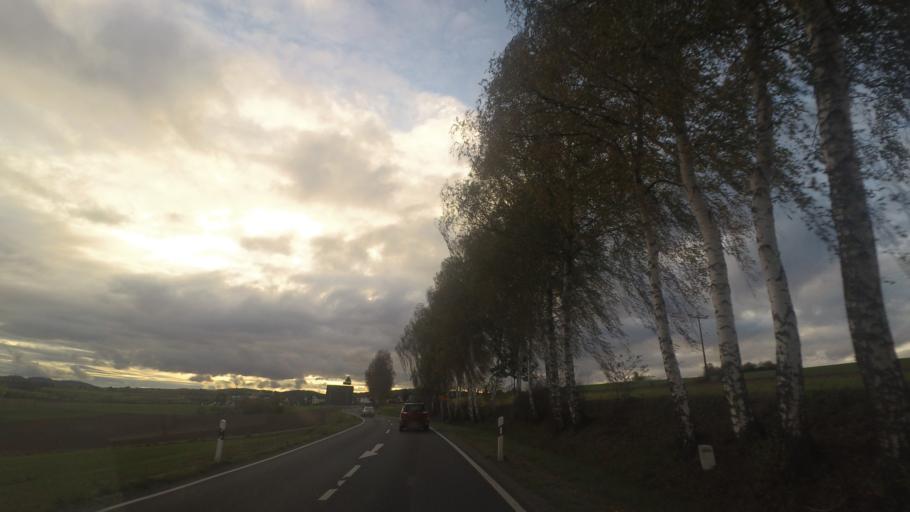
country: DE
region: Hesse
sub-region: Regierungsbezirk Kassel
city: Neuhof
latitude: 50.4546
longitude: 9.5909
